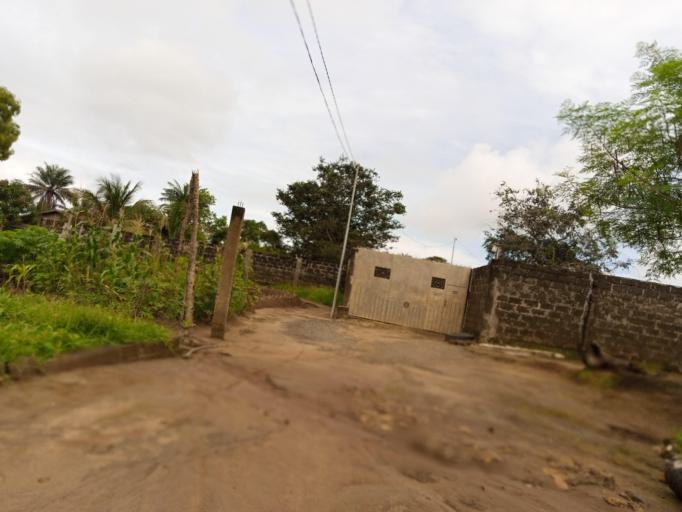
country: SL
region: Northern Province
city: Masoyila
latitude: 8.5990
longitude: -13.1965
